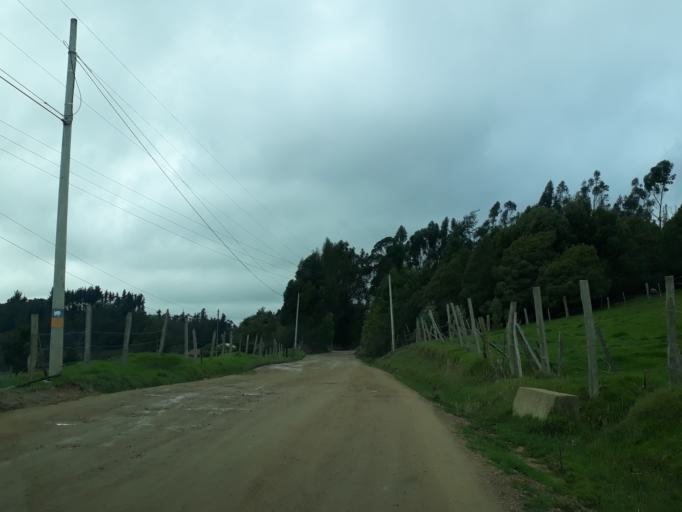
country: CO
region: Cundinamarca
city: Cucunuba
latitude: 5.1985
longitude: -73.7776
